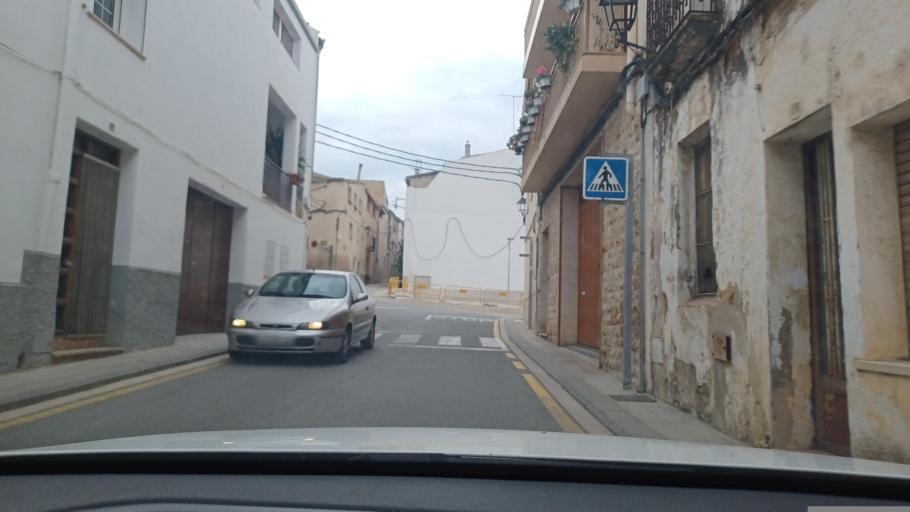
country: ES
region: Catalonia
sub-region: Provincia de Tarragona
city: Ulldecona
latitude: 40.6564
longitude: 0.4683
